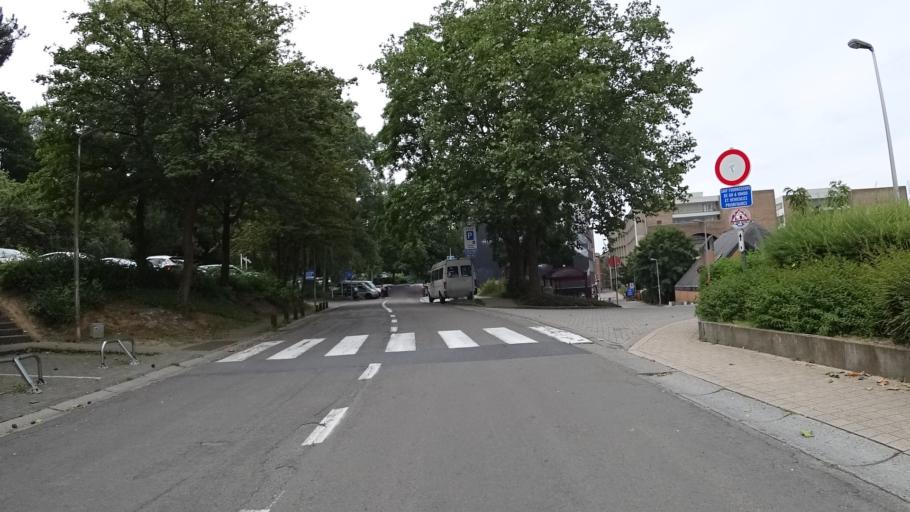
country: BE
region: Wallonia
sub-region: Province du Brabant Wallon
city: Louvain-la-Neuve
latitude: 50.6705
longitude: 4.6179
